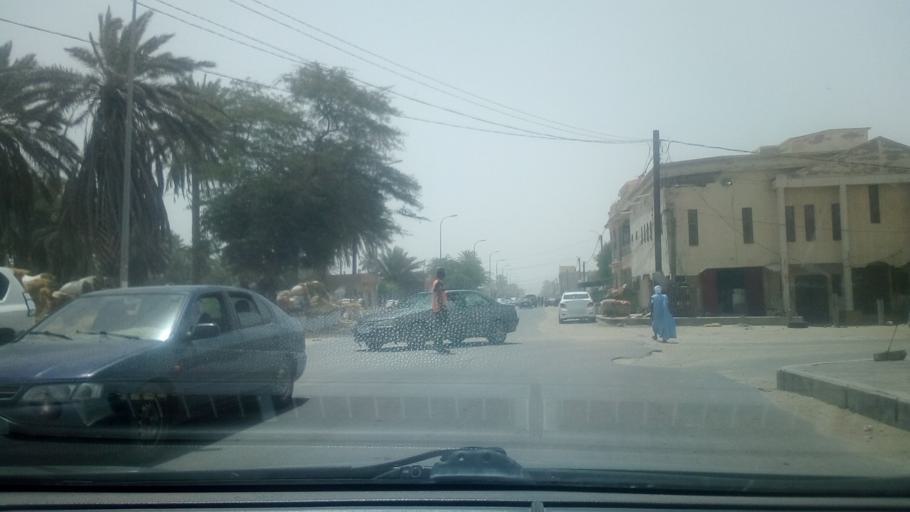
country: MR
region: Nouakchott
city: Nouakchott
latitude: 18.0833
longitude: -15.9902
